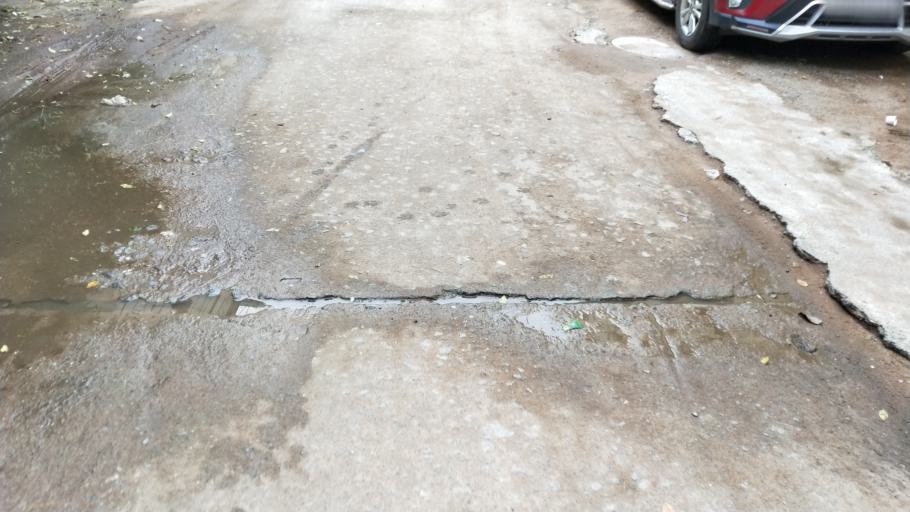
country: IN
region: Telangana
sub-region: Rangareddi
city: Kukatpalli
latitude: 17.4926
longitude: 78.4073
